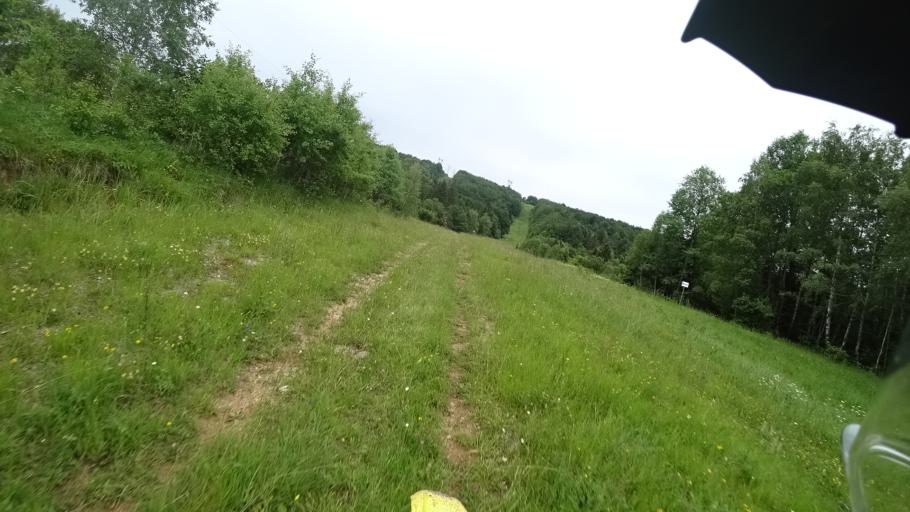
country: HR
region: Primorsko-Goranska
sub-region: Grad Delnice
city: Delnice
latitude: 45.3796
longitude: 14.8883
